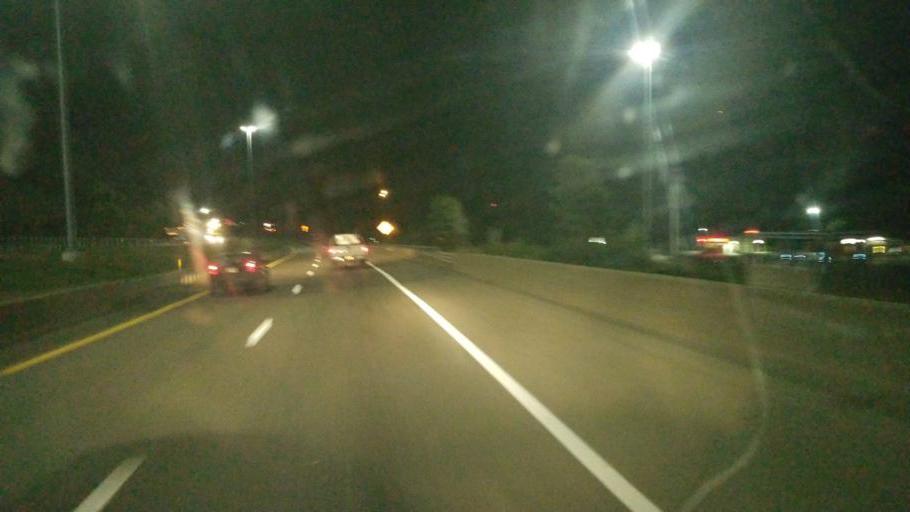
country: US
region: West Virginia
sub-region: Ohio County
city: West Liberty
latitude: 40.0672
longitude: -80.5681
